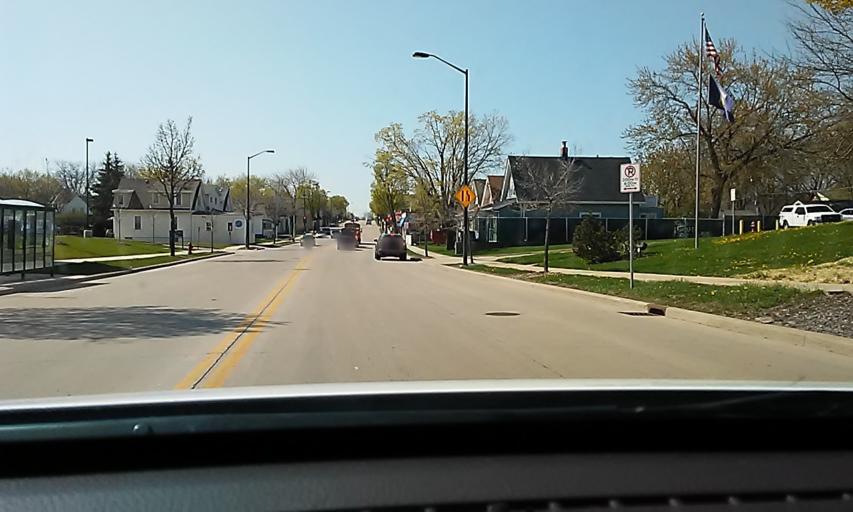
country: US
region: Wisconsin
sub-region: Milwaukee County
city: West Milwaukee
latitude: 43.0221
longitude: -87.9876
